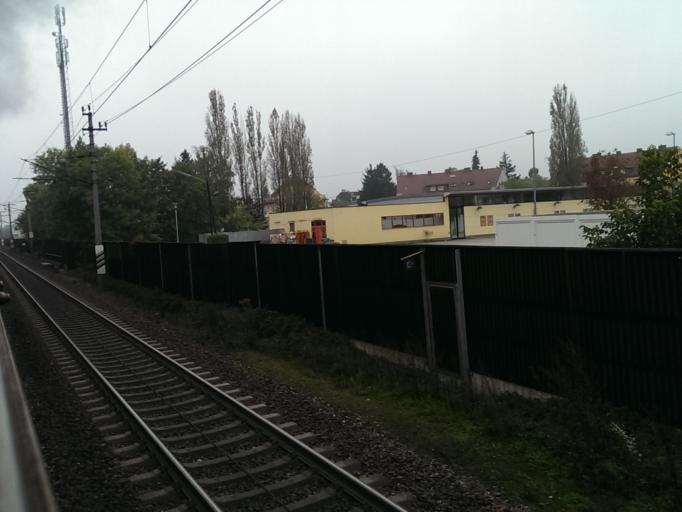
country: AT
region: Upper Austria
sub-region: Wels Stadt
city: Wels
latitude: 48.1630
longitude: 14.0166
